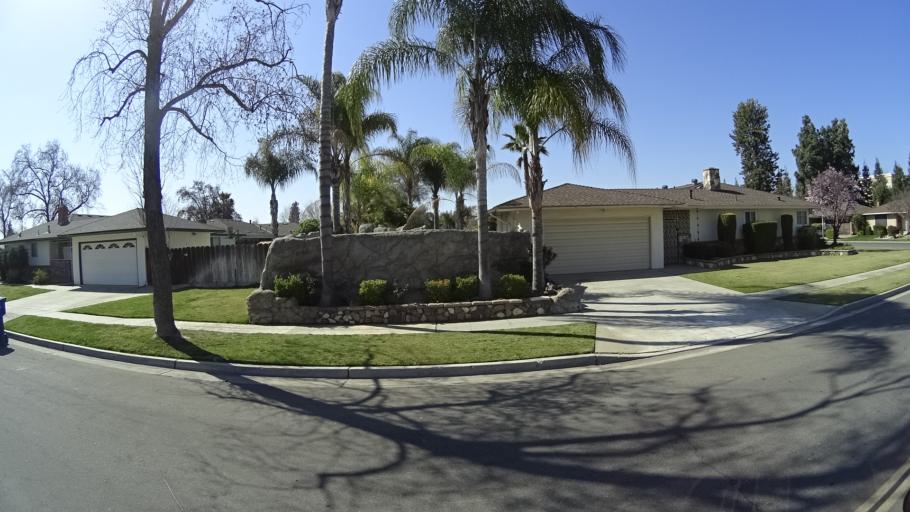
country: US
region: California
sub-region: Fresno County
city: Clovis
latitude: 36.8349
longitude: -119.7773
